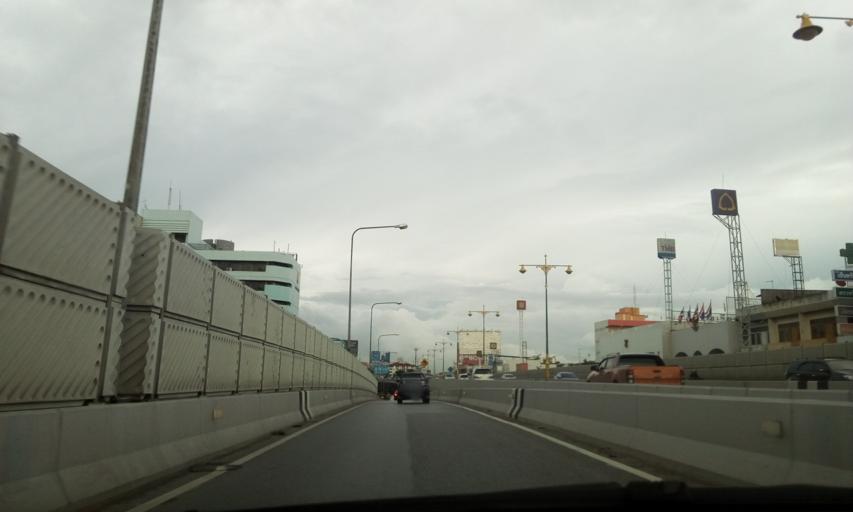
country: TH
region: Nonthaburi
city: Pak Kret
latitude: 13.9130
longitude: 100.4966
